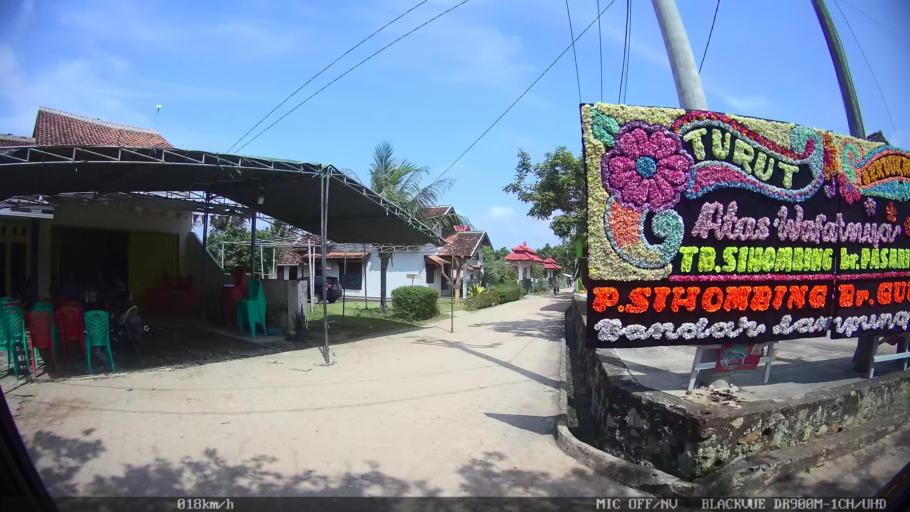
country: ID
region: Lampung
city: Kedaton
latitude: -5.3411
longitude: 105.2711
